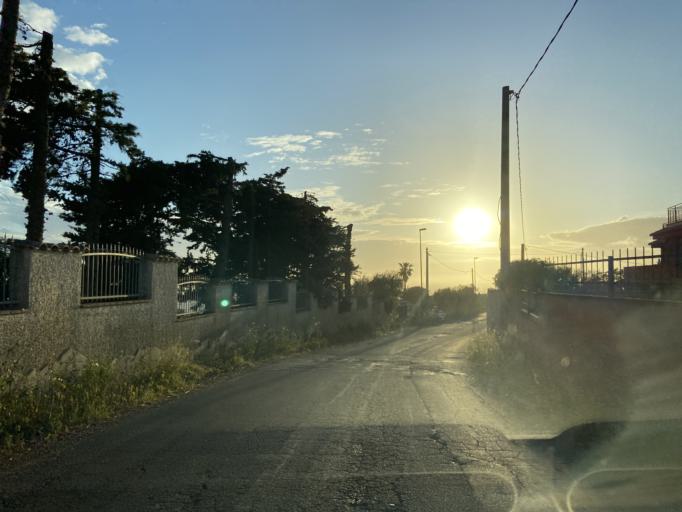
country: IT
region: Latium
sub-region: Citta metropolitana di Roma Capitale
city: Civitavecchia
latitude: 42.0815
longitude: 11.8326
